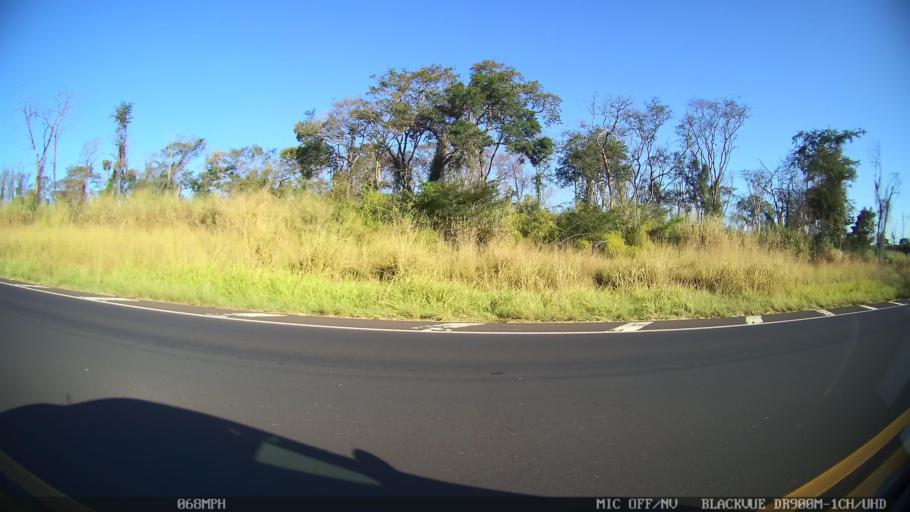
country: BR
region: Sao Paulo
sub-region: Guapiacu
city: Guapiacu
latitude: -20.7426
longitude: -49.1033
